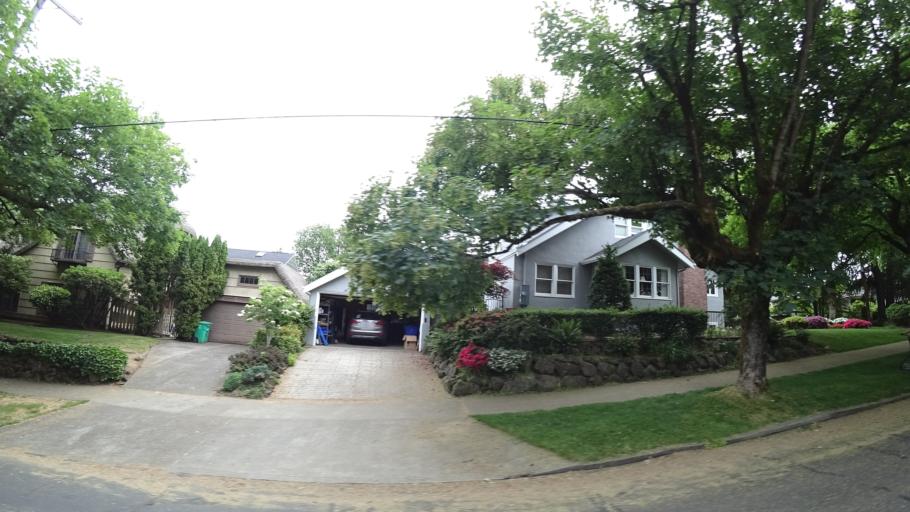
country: US
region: Oregon
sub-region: Multnomah County
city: Portland
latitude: 45.5284
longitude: -122.6210
